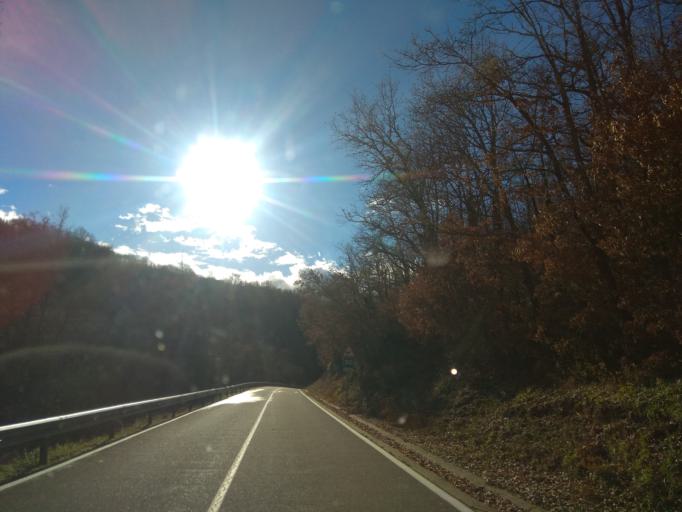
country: ES
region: Cantabria
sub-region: Provincia de Cantabria
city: San Martin de Elines
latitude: 42.9040
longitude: -3.8835
